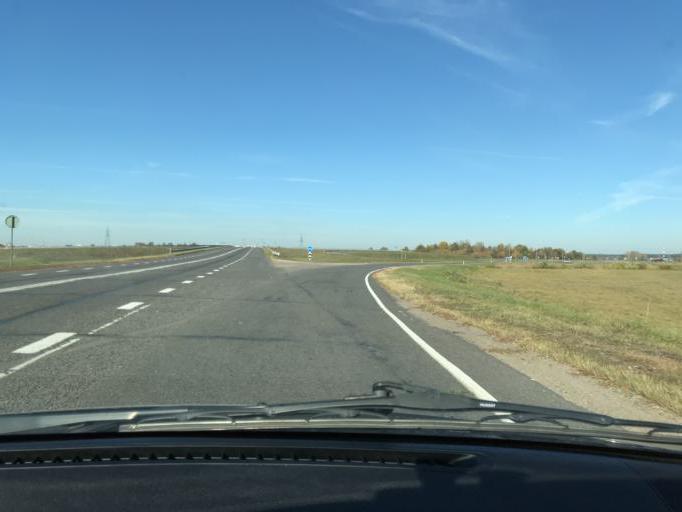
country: BY
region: Brest
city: Ivatsevichy
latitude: 52.6962
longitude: 25.3645
